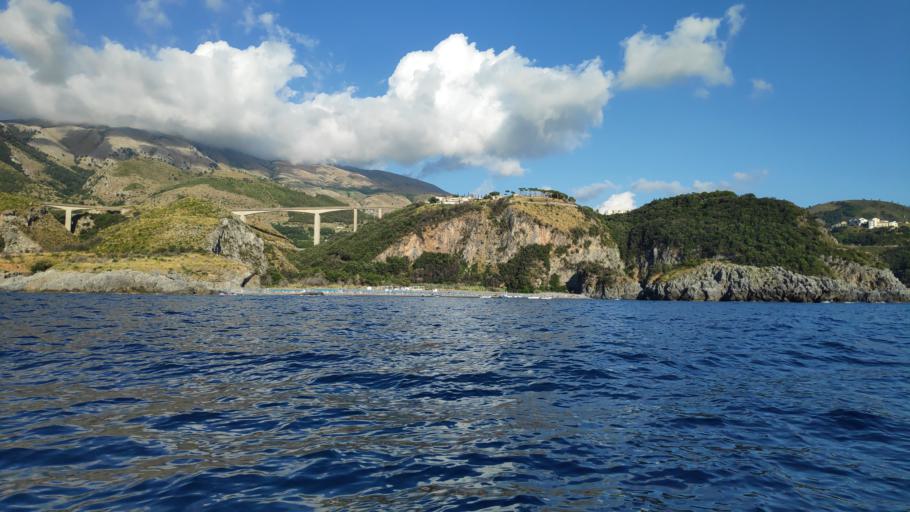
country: IT
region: Calabria
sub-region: Provincia di Cosenza
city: San Nicola Arcella
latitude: 39.8590
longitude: 15.7860
